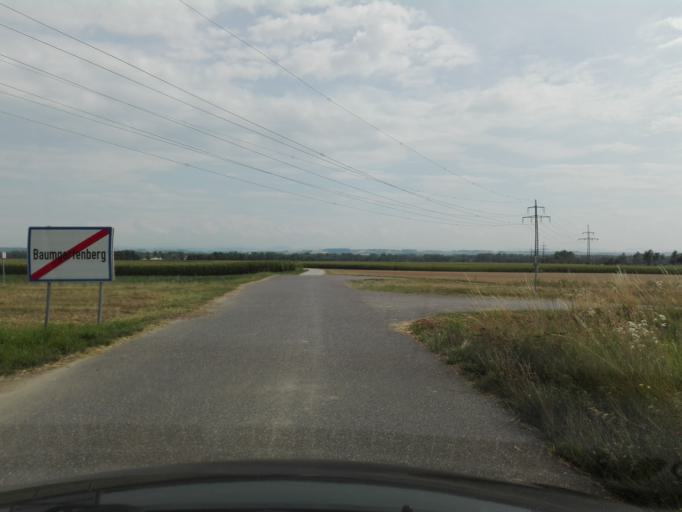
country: AT
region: Upper Austria
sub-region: Politischer Bezirk Perg
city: Bad Kreuzen
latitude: 48.2056
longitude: 14.7598
